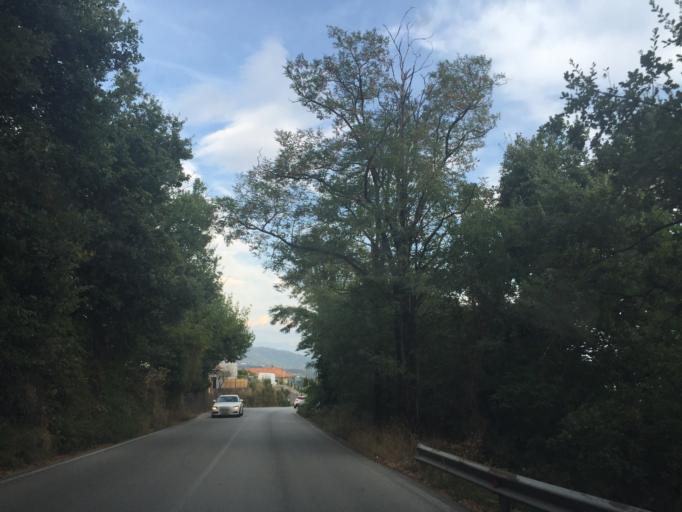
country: IT
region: Tuscany
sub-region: Provincia di Pistoia
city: Campo Tizzoro
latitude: 43.9793
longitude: 10.8709
